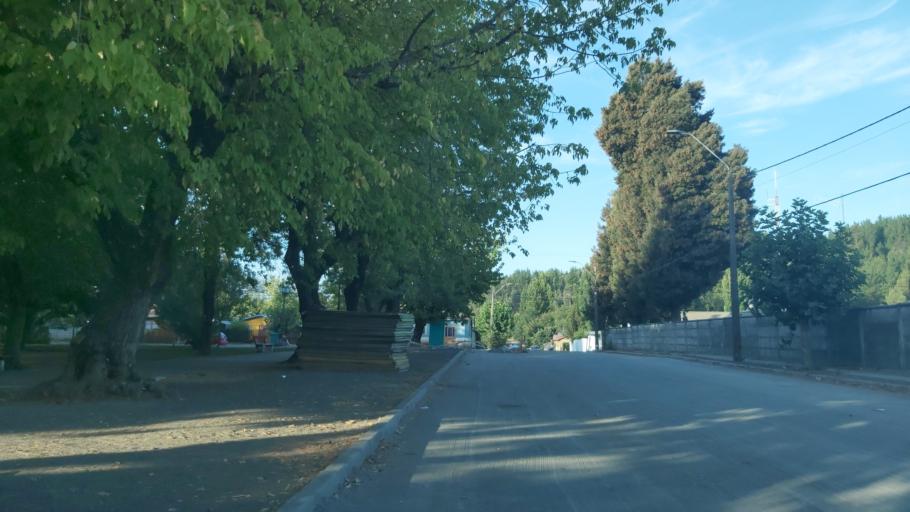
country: CL
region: Biobio
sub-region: Provincia de Biobio
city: La Laja
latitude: -37.1628
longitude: -72.9071
